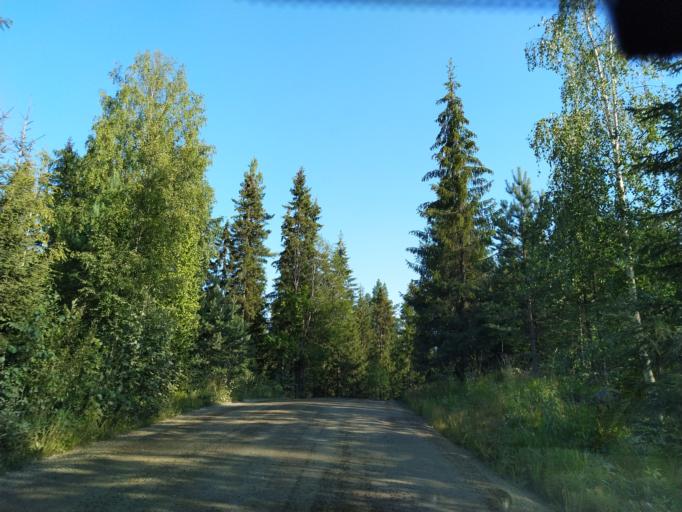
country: FI
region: Central Finland
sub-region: Jaemsae
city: Kuhmoinen
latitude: 61.6297
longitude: 25.0930
